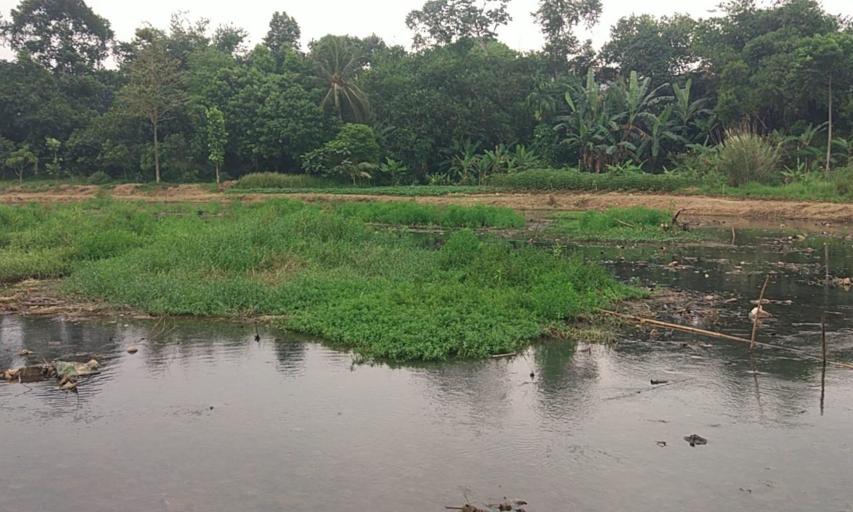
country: ID
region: West Java
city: Ciampea
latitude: -6.5123
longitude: 106.7704
